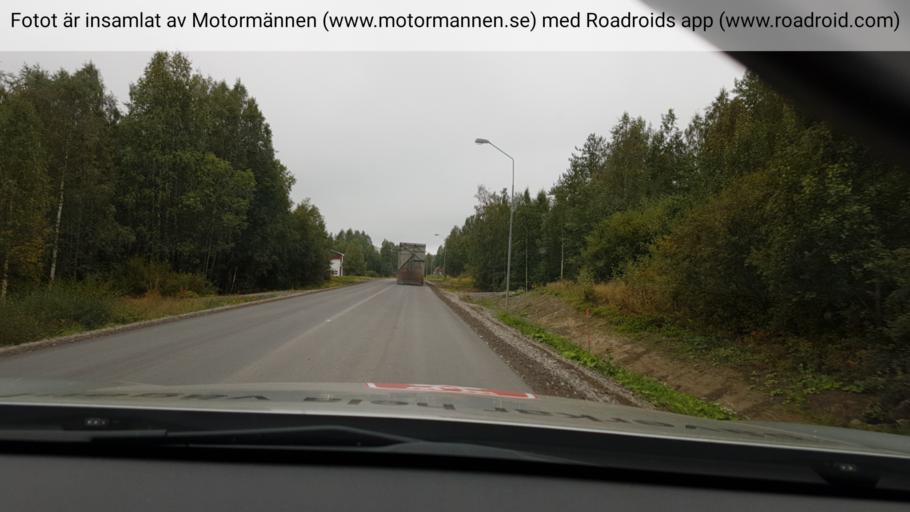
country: SE
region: Vaesterbotten
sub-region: Skelleftea Kommun
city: Burtraesk
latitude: 64.3569
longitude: 20.5054
